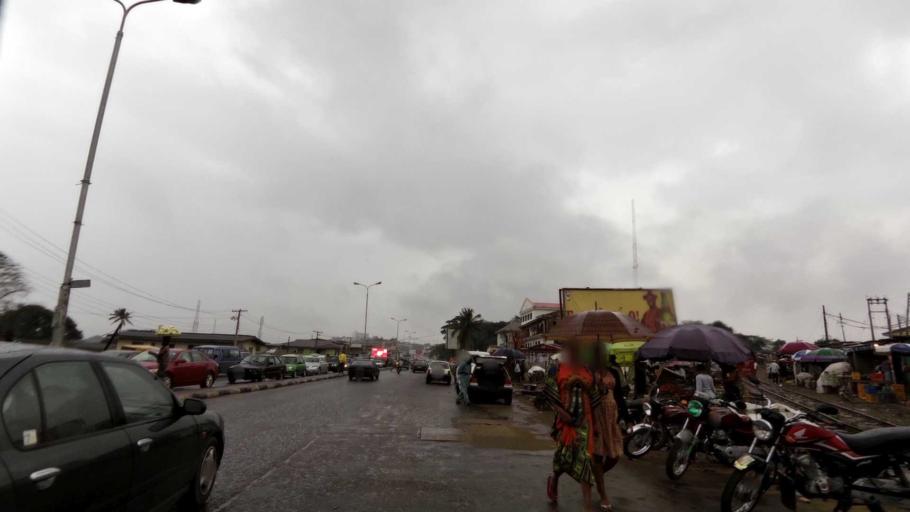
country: NG
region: Oyo
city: Ibadan
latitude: 7.4208
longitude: 3.8972
